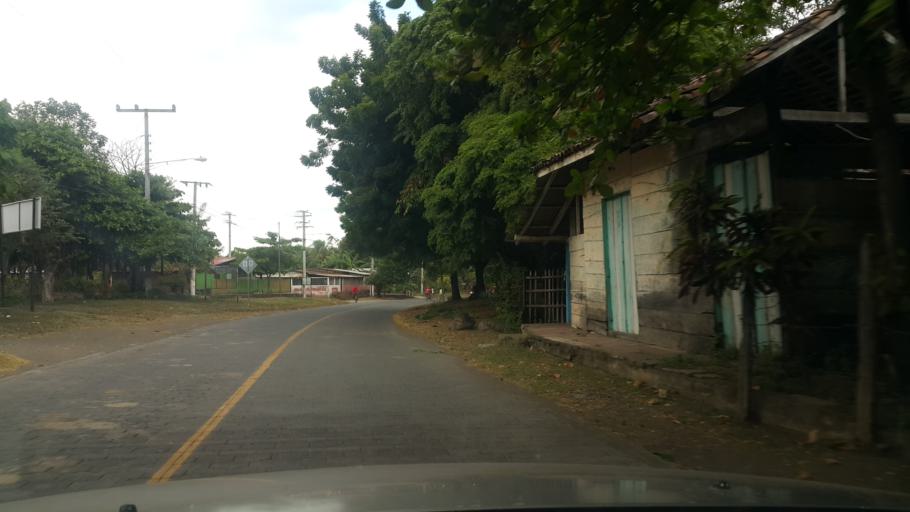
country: NI
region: Rivas
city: Moyogalpa
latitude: 11.5086
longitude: -85.7063
